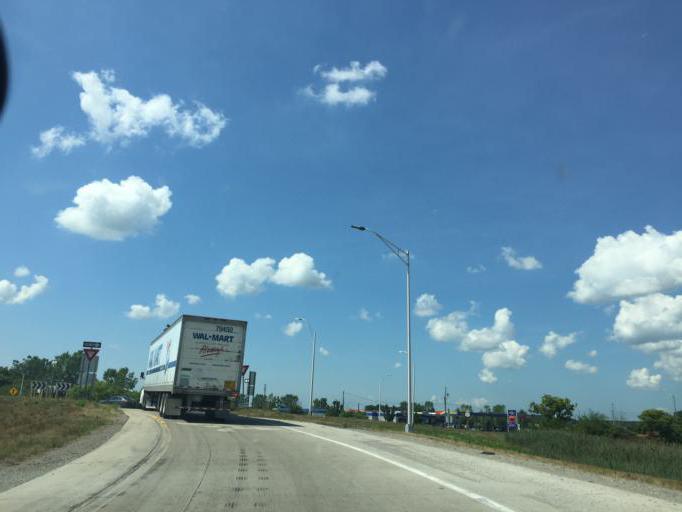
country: US
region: Michigan
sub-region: Monroe County
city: Lambertville
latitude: 41.7986
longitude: -83.6899
